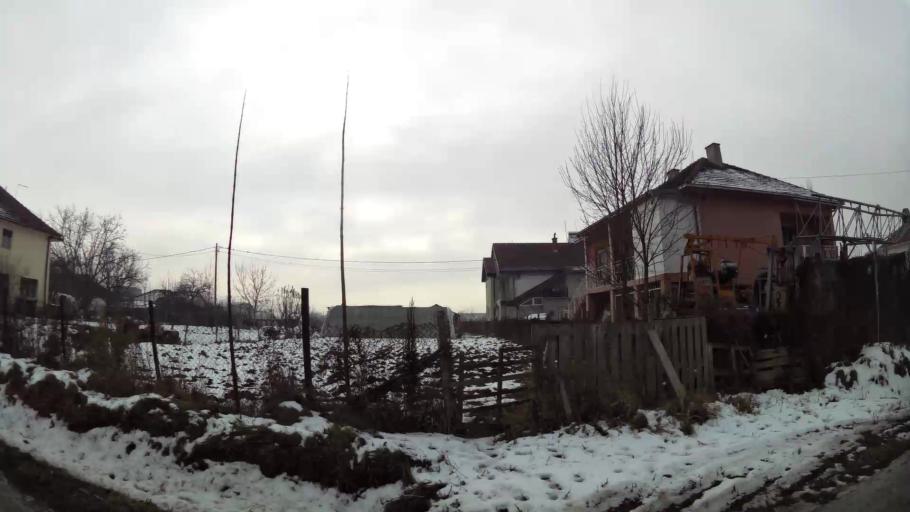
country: MK
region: Ilinden
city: Ilinden
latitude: 41.9913
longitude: 21.5756
